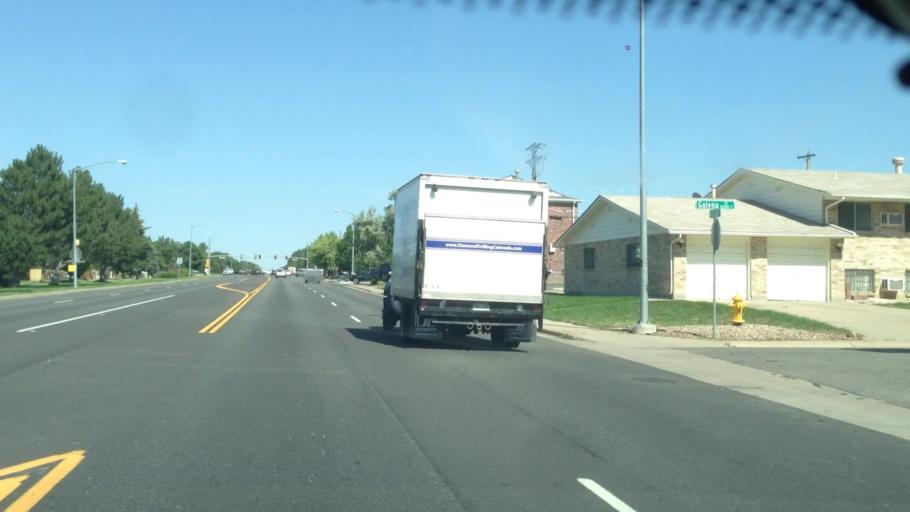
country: US
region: Colorado
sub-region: Adams County
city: Aurora
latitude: 39.7256
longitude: -104.8696
